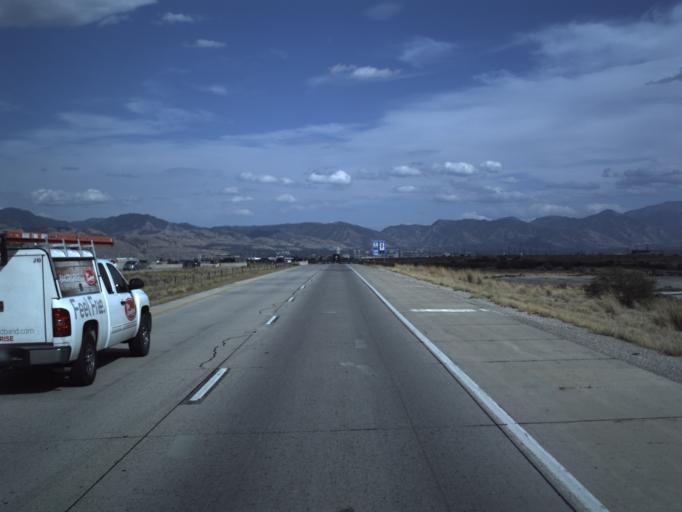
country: US
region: Utah
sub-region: Salt Lake County
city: Magna
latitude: 40.7709
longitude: -112.0416
